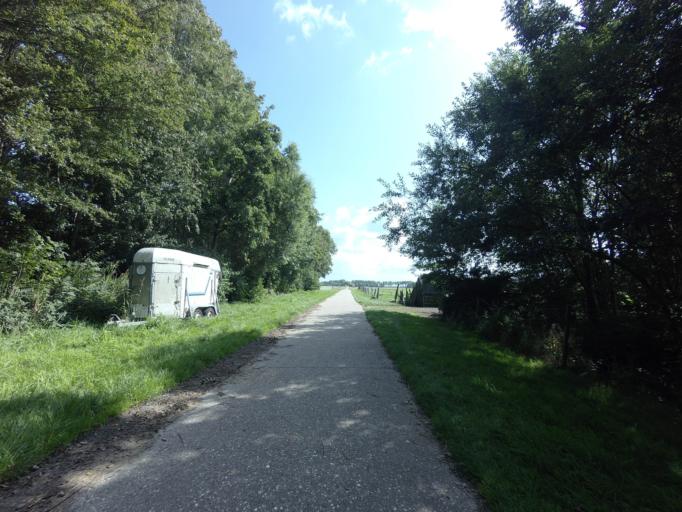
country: NL
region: Friesland
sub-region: Gemeente Het Bildt
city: Sint Annaparochie
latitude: 53.2822
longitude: 5.7053
